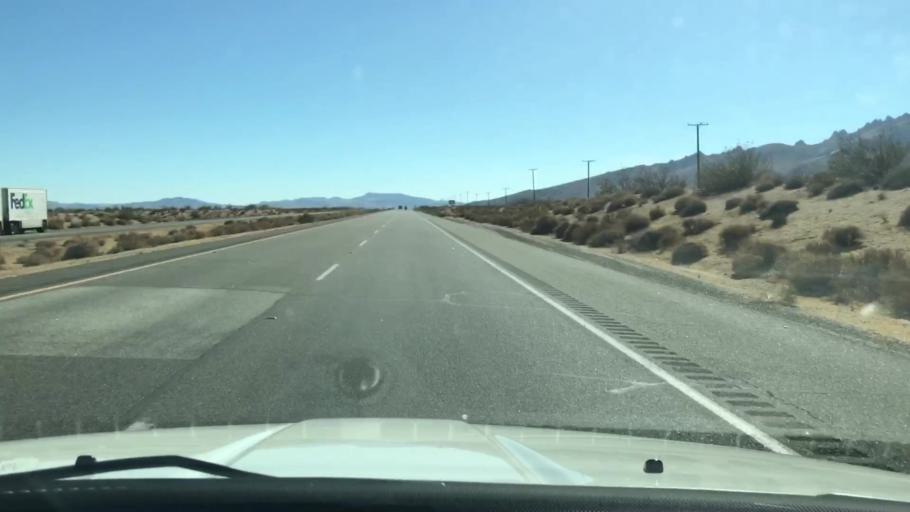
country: US
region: California
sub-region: Kern County
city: Inyokern
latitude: 35.7479
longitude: -117.8703
